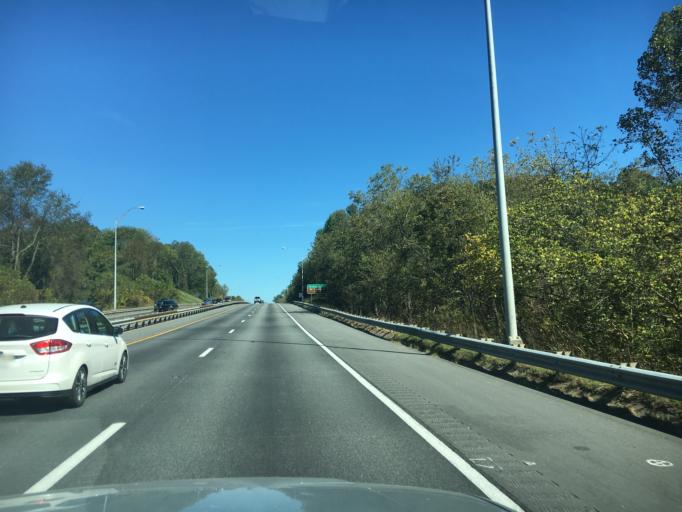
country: US
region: North Carolina
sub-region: Buncombe County
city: Bent Creek
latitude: 35.5605
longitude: -82.6043
